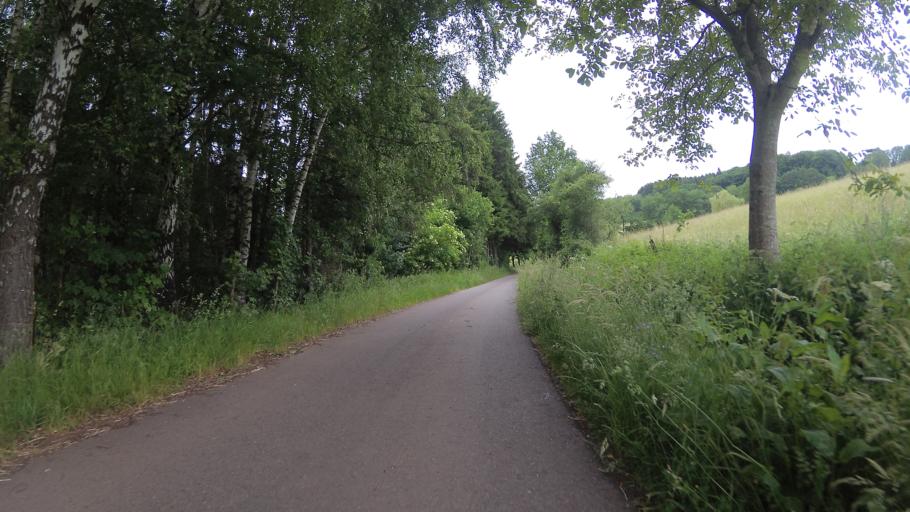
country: DE
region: Saarland
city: Hangard
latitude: 49.4157
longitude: 7.2156
